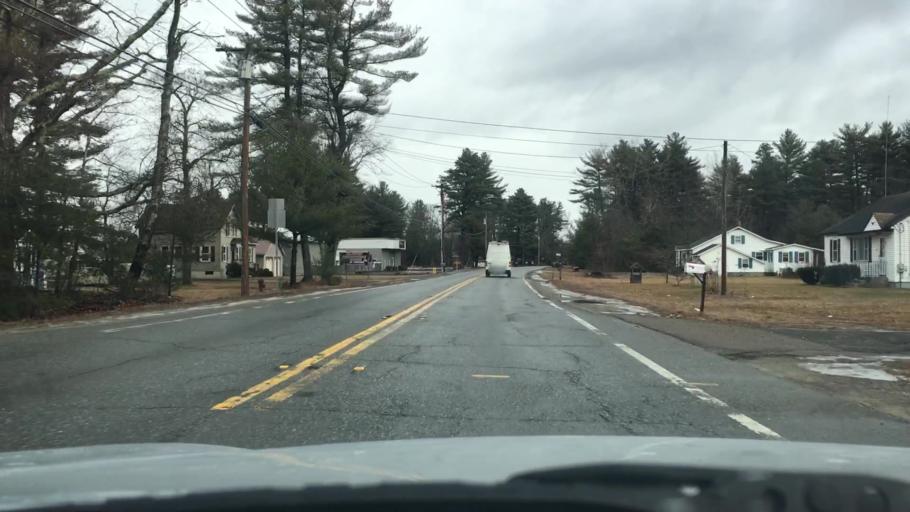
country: US
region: Massachusetts
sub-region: Franklin County
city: Orange
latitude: 42.5622
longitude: -72.2819
